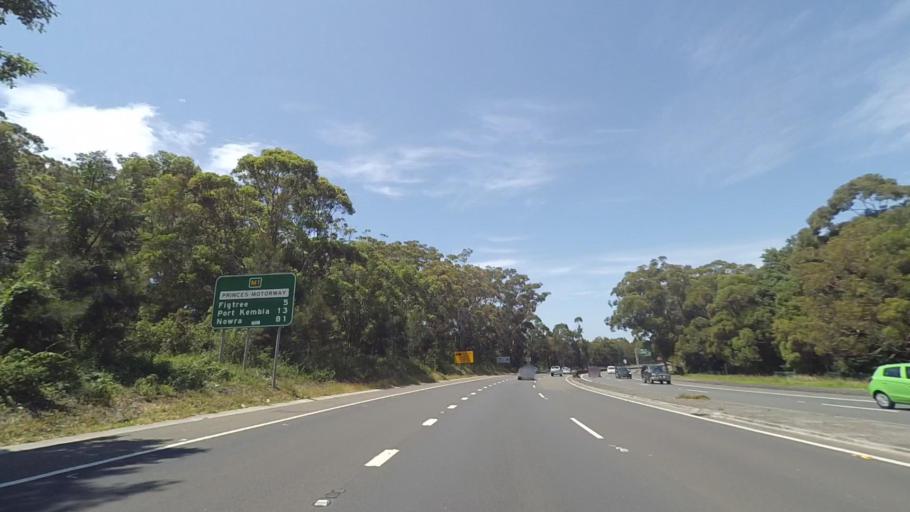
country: AU
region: New South Wales
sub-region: Wollongong
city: Mount Ousley
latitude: -34.4026
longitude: 150.8823
